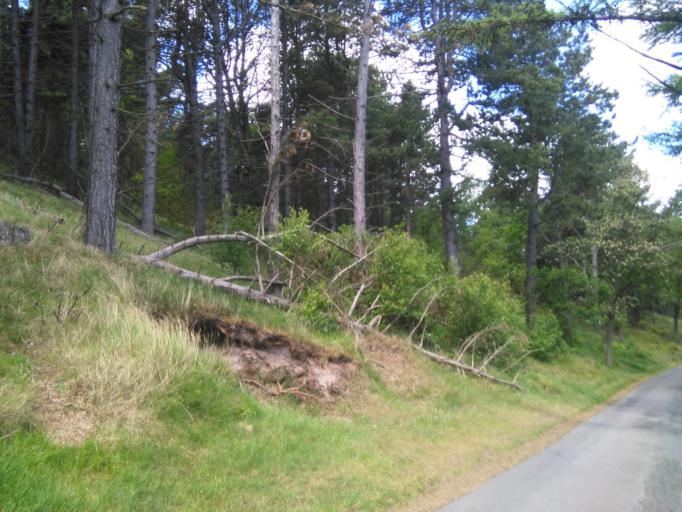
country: DK
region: Capital Region
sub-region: Bornholm Kommune
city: Ronne
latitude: 55.2966
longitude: 14.7762
